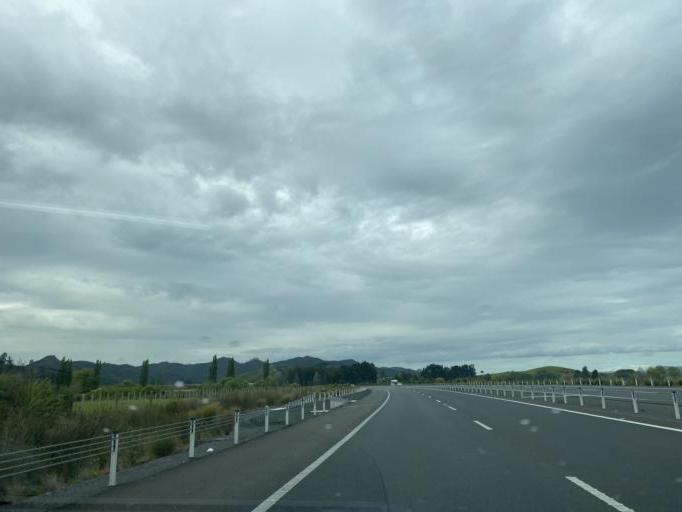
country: NZ
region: Waikato
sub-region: Waikato District
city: Ngaruawahia
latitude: -37.6043
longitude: 175.2055
